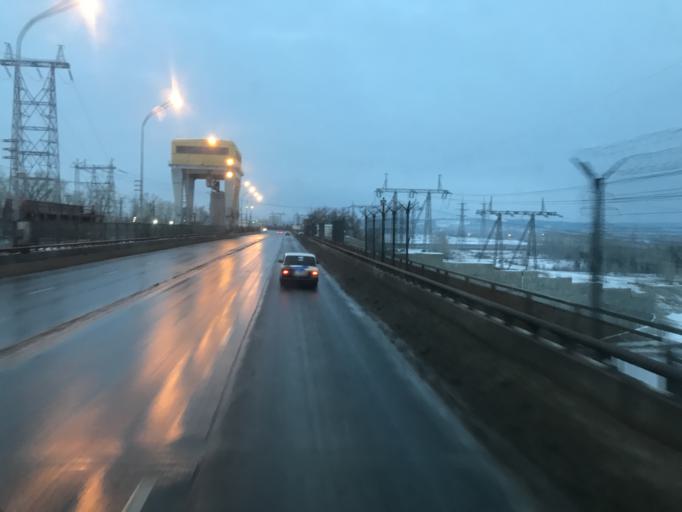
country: RU
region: Samara
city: Zhigulevsk
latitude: 53.4593
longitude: 49.4988
